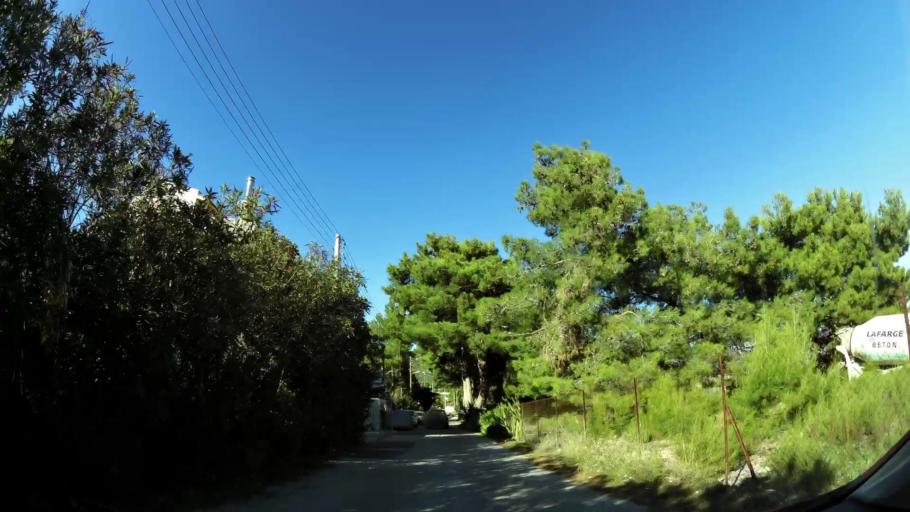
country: GR
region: Attica
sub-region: Nomarchia Anatolikis Attikis
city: Leondarion
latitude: 37.9945
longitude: 23.8446
